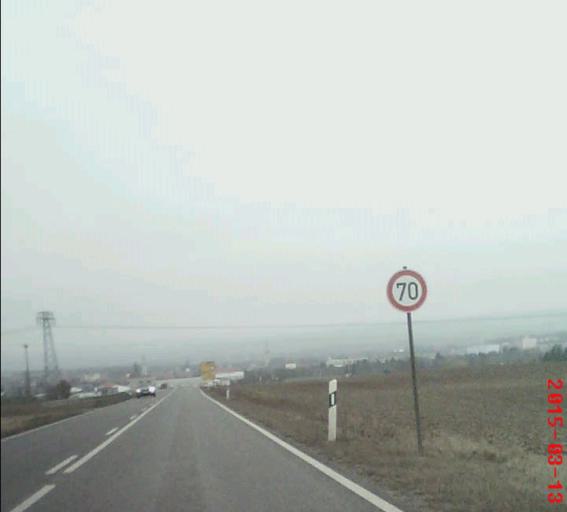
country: DE
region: Thuringia
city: Bad Langensalza
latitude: 51.0886
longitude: 10.6422
